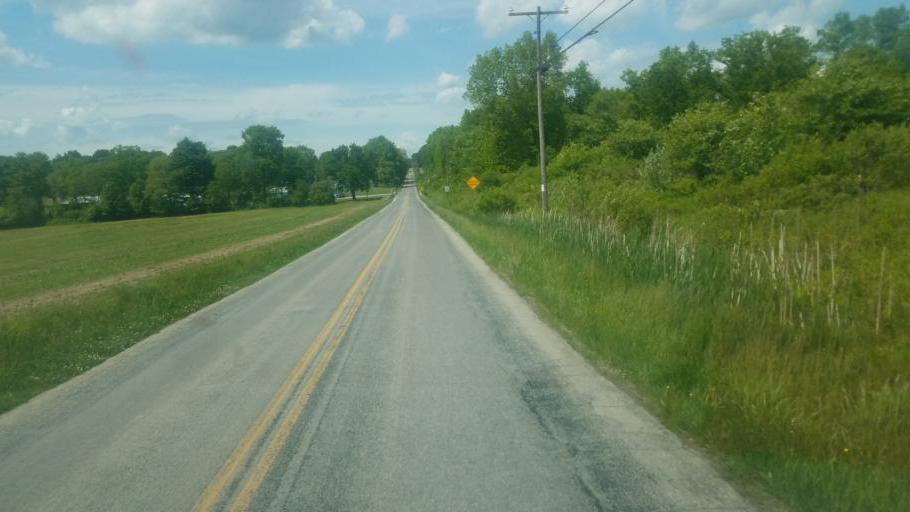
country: US
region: Pennsylvania
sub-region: Venango County
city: Franklin
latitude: 41.2184
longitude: -79.8456
